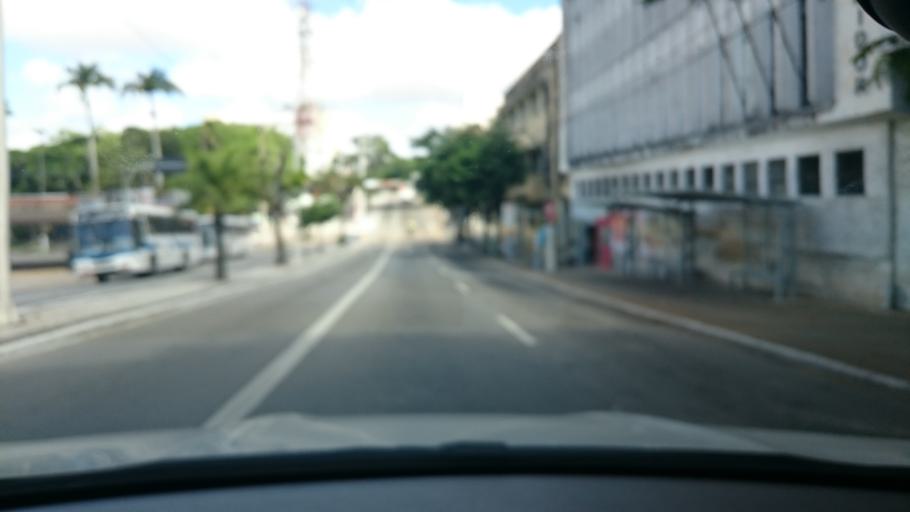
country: BR
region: Paraiba
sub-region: Campina Grande
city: Campina Grande
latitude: -7.2191
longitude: -35.8831
